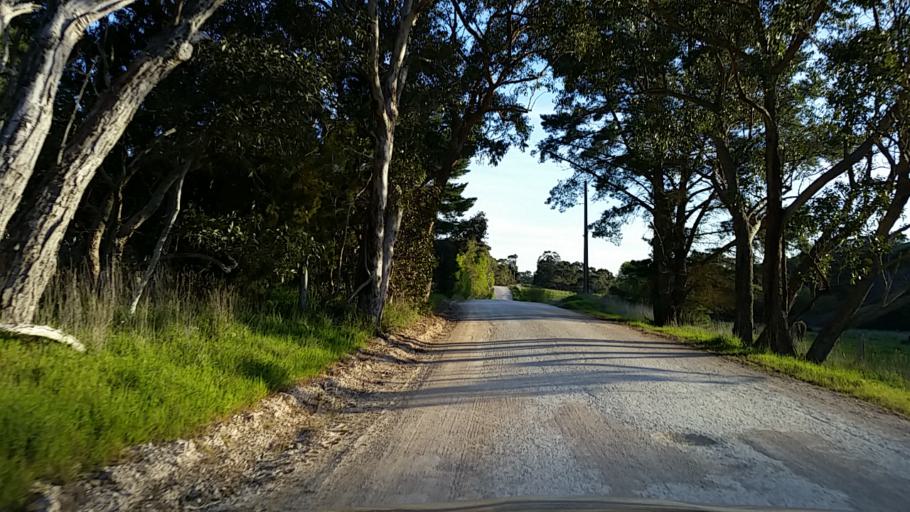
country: AU
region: South Australia
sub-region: Alexandrina
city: Mount Compass
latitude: -35.2895
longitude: 138.6900
